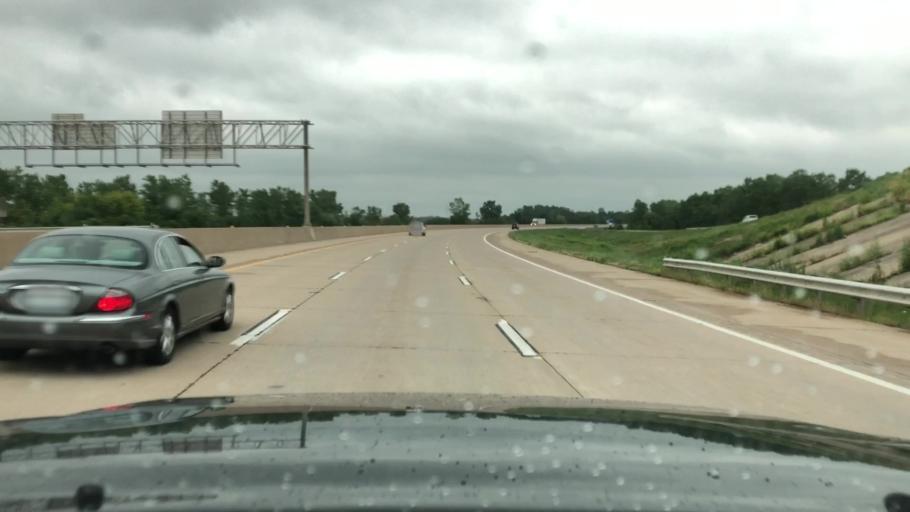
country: US
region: Missouri
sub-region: Saint Charles County
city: Saint Peters
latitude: 38.8117
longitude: -90.5855
